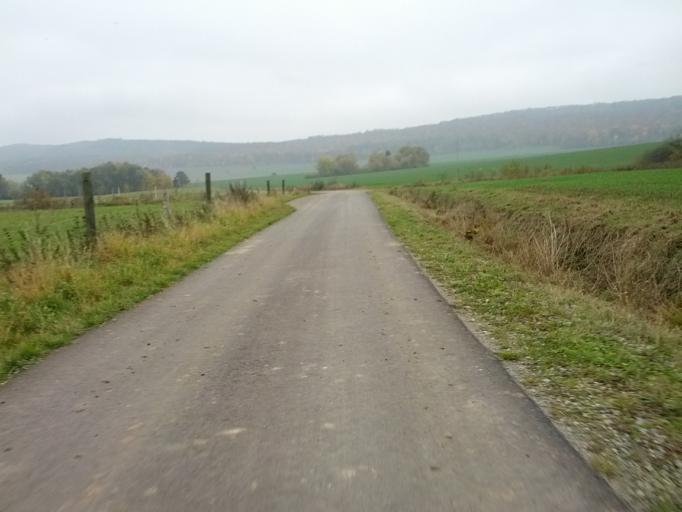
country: DE
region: Thuringia
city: Seebach
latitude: 50.9833
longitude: 10.4157
